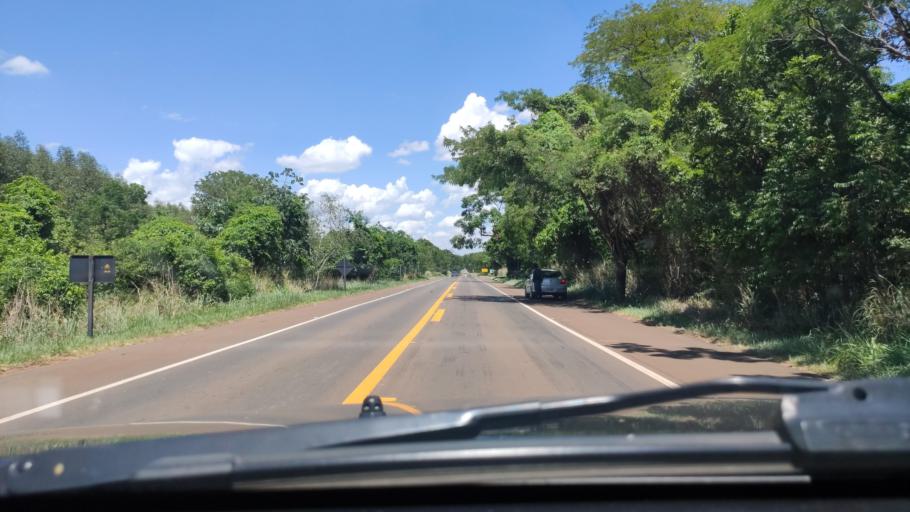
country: BR
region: Sao Paulo
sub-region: Boa Esperanca Do Sul
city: Boa Esperanca do Sul
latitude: -22.0690
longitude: -48.3710
